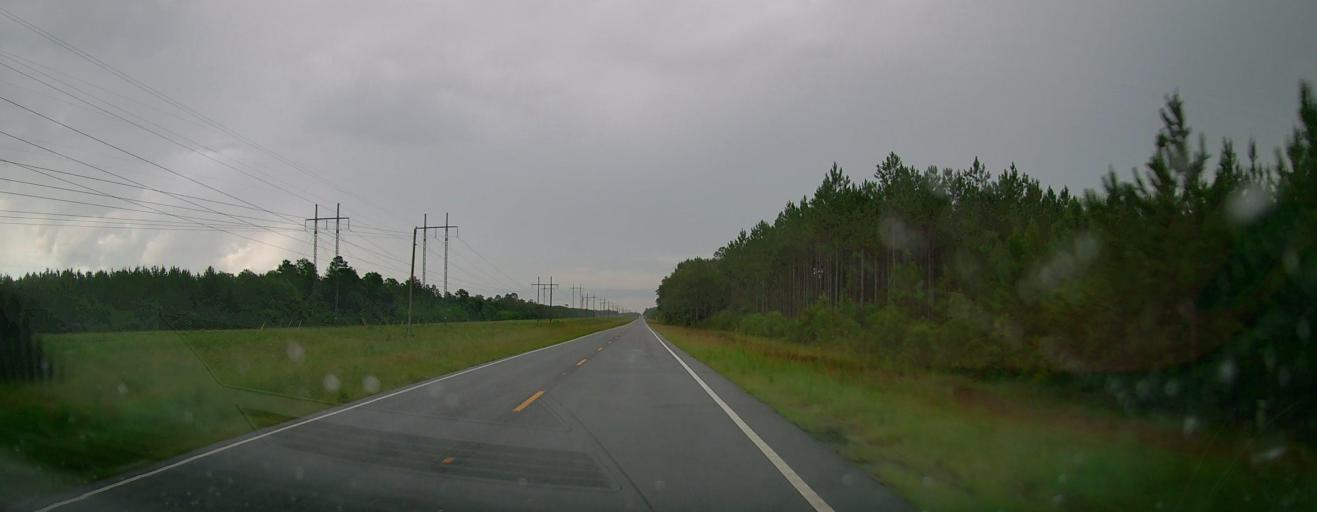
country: US
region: Georgia
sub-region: Brantley County
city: Nahunta
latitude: 31.3356
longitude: -81.8815
